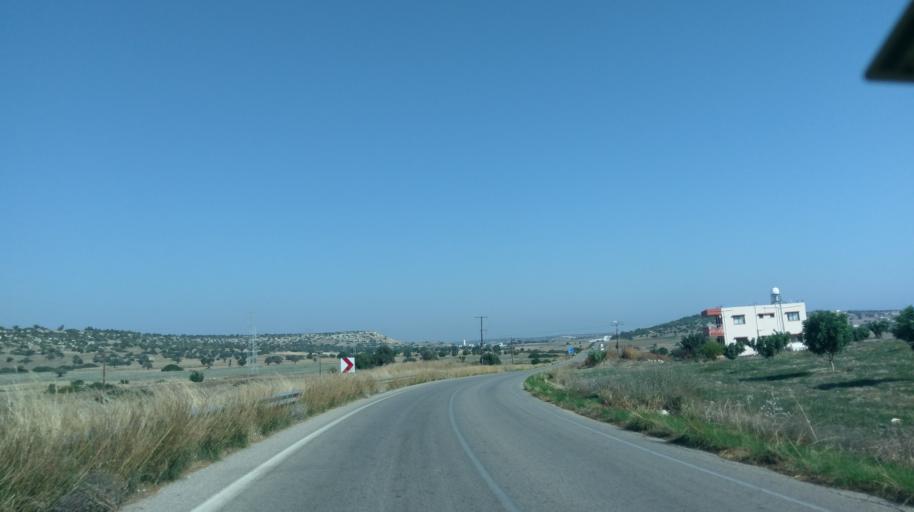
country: CY
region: Ammochostos
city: Leonarisso
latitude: 35.3942
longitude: 34.0614
